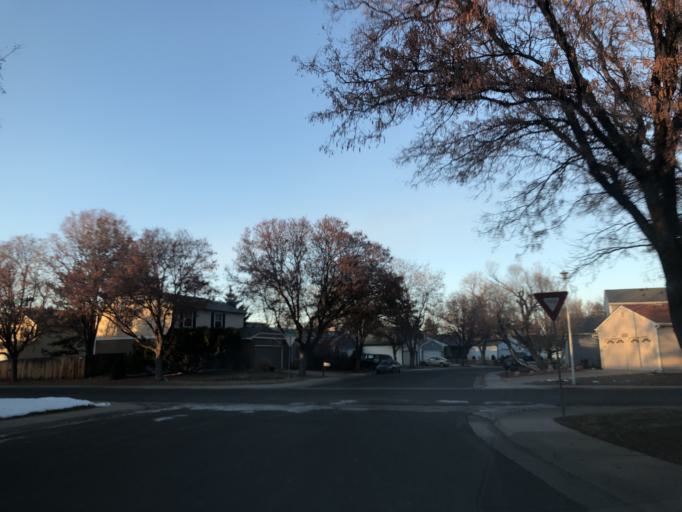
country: US
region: Colorado
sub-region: Adams County
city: Aurora
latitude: 39.7035
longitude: -104.8038
